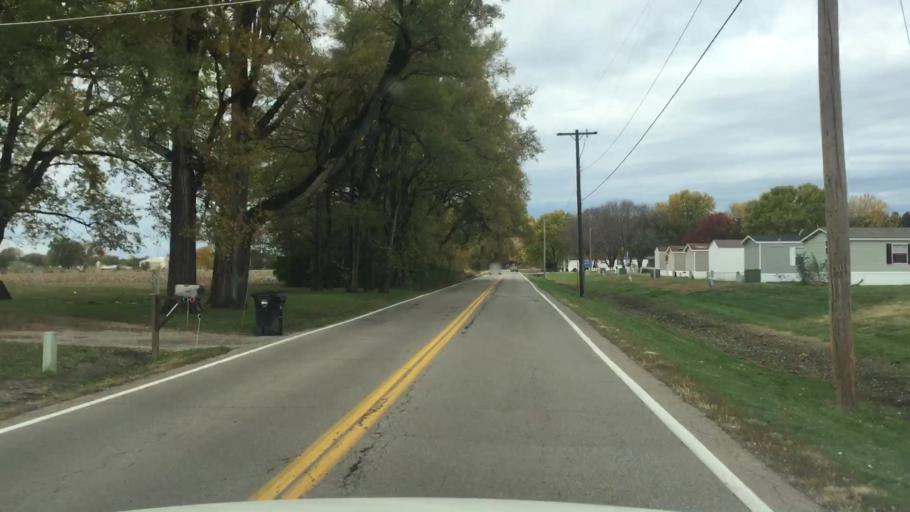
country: US
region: Kansas
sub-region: Shawnee County
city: Topeka
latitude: 39.0877
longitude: -95.6887
